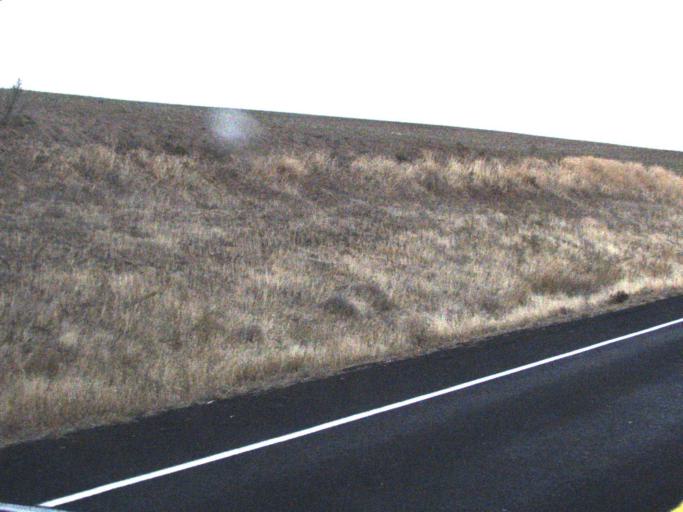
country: US
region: Washington
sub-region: Garfield County
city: Pomeroy
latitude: 46.7922
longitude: -117.8904
